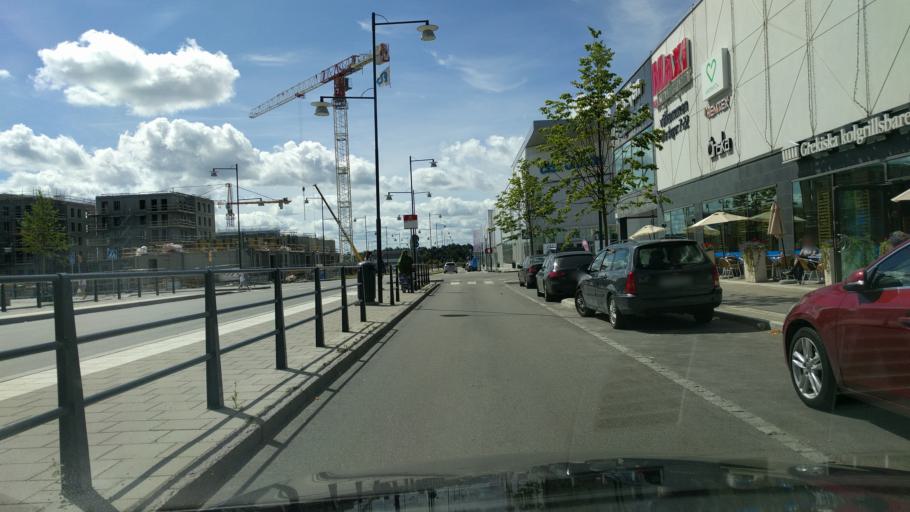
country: SE
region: Stockholm
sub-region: Jarfalla Kommun
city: Jakobsberg
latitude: 59.4138
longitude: 17.8646
